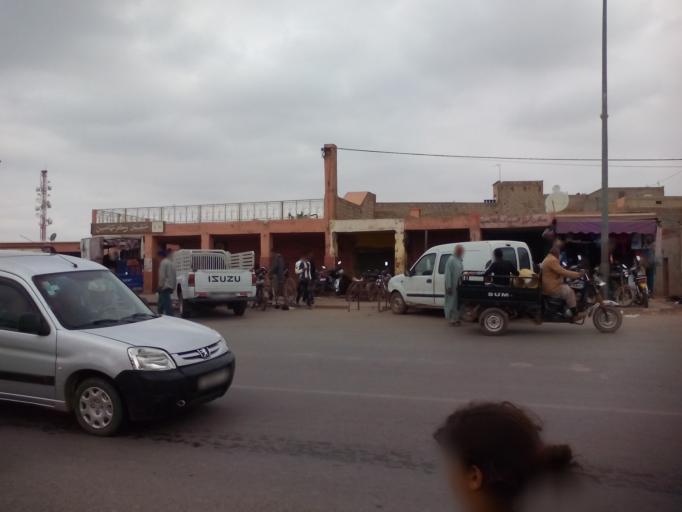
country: MA
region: Marrakech-Tensift-Al Haouz
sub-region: Marrakech
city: Marrakesh
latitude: 31.6344
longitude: -8.2487
